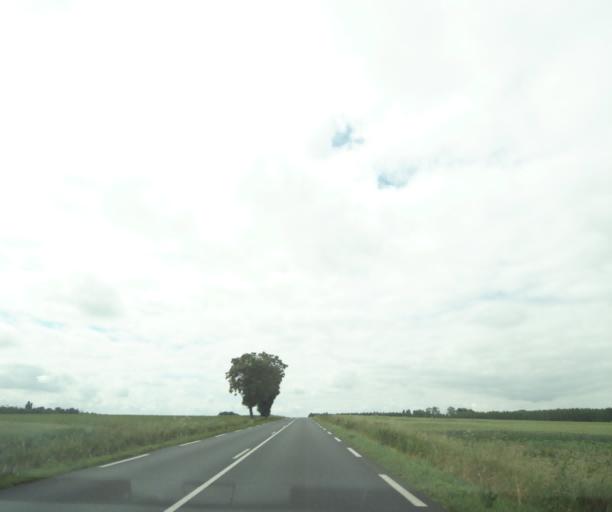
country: FR
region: Pays de la Loire
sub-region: Departement de Maine-et-Loire
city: Montreuil-Bellay
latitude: 47.1141
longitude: -0.1627
